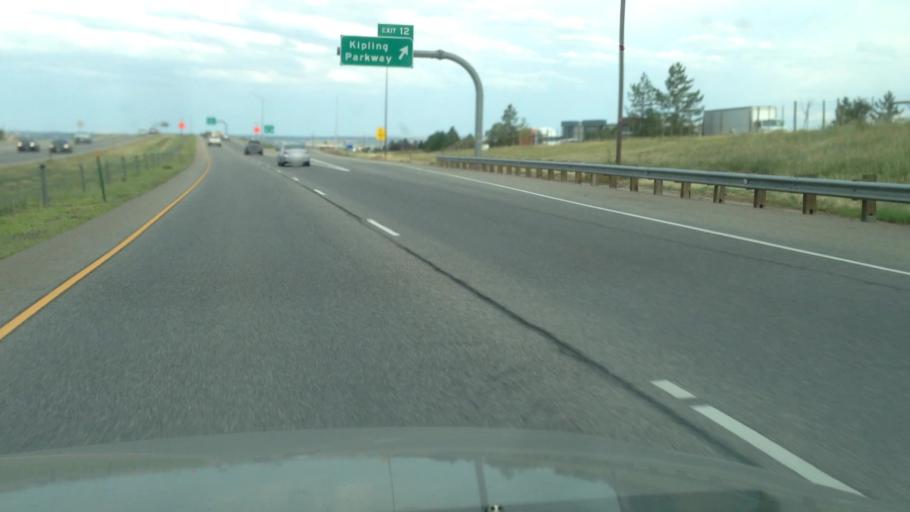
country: US
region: Colorado
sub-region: Jefferson County
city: Ken Caryl
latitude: 39.5602
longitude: -105.1161
